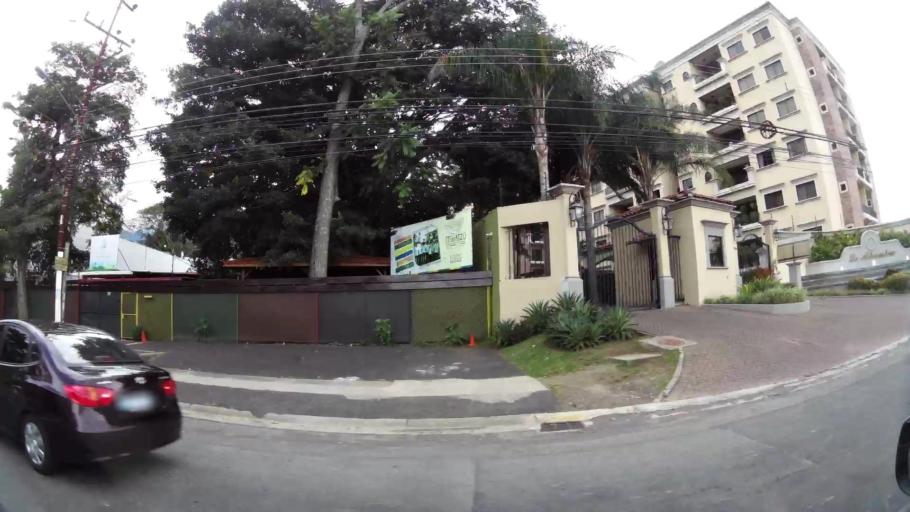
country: CR
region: San Jose
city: San Rafael
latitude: 9.9334
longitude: -84.1531
